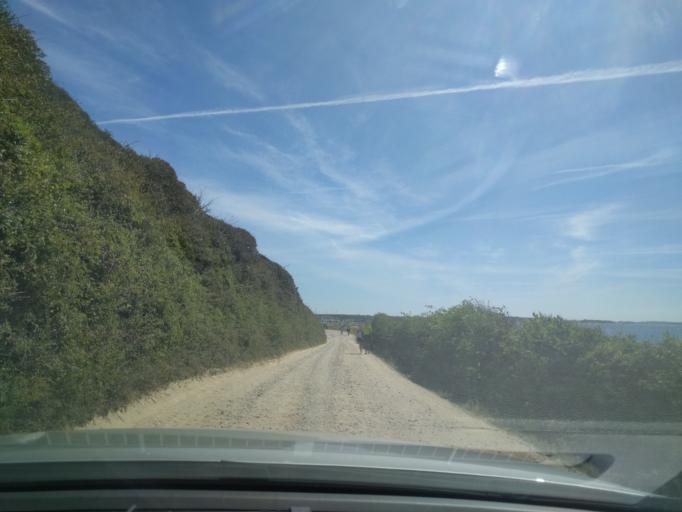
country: DK
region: South Denmark
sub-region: Kerteminde Kommune
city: Munkebo
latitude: 55.6086
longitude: 10.6013
